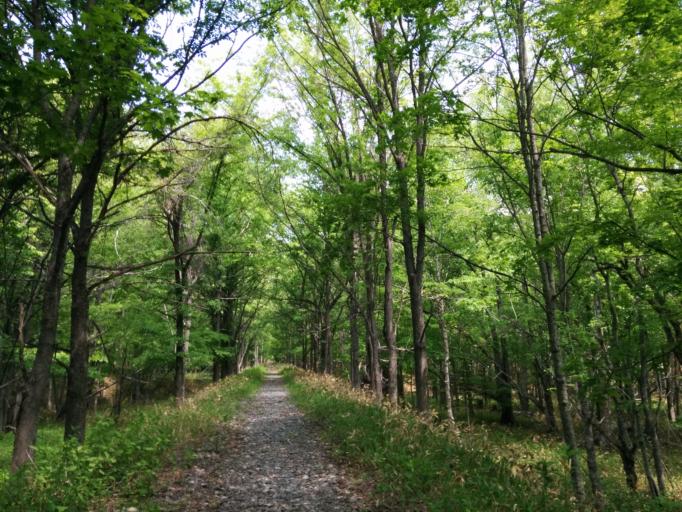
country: JP
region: Hokkaido
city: Otofuke
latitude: 43.4005
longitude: 143.1826
